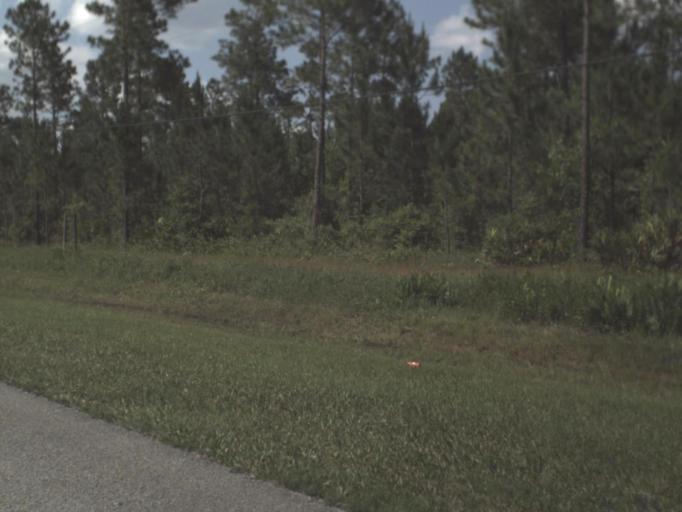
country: US
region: Florida
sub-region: Alachua County
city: Waldo
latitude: 29.7072
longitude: -82.1357
